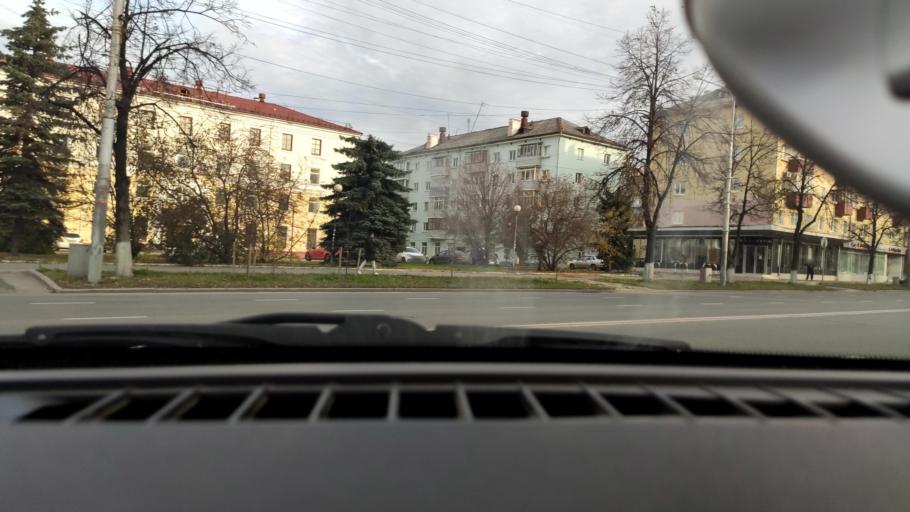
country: RU
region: Perm
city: Perm
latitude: 58.0061
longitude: 56.2091
